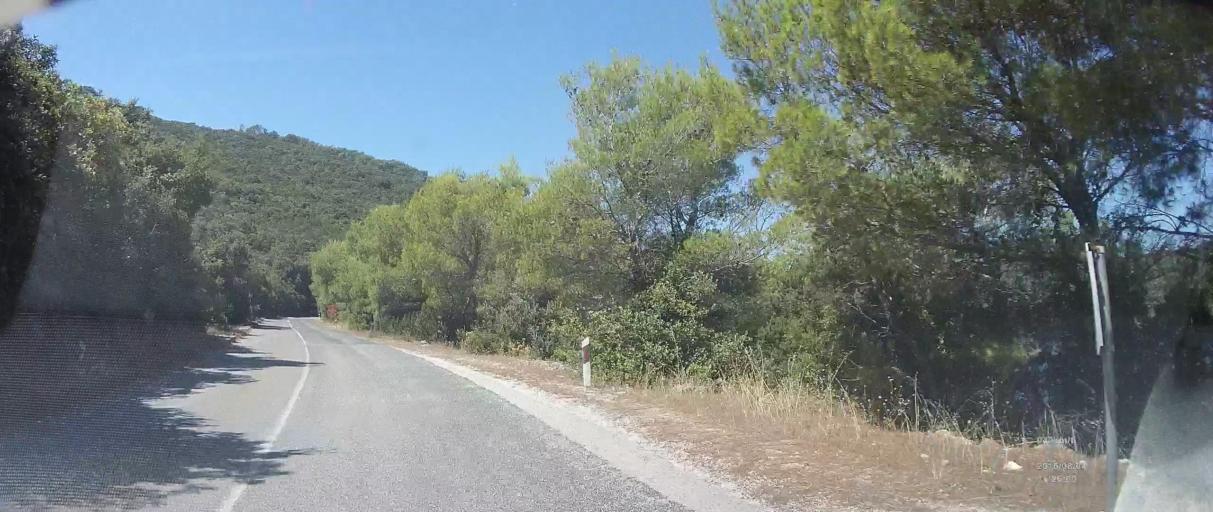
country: HR
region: Dubrovacko-Neretvanska
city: Blato
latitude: 42.7872
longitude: 17.3918
